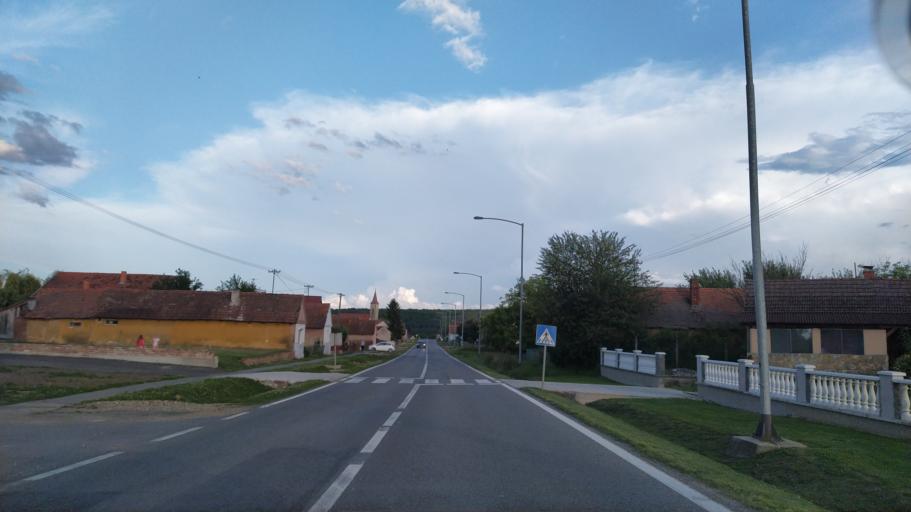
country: HR
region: Osjecko-Baranjska
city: Fericanci
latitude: 45.4984
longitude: 18.0149
